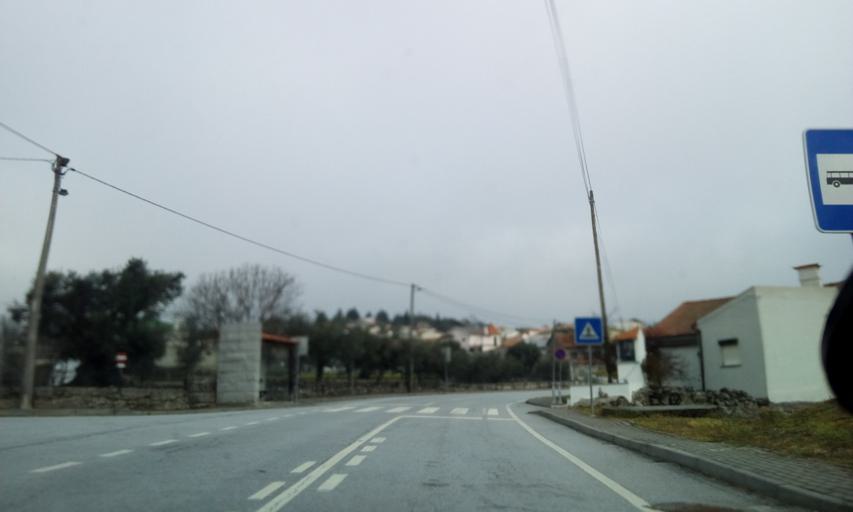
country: PT
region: Guarda
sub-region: Fornos de Algodres
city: Fornos de Algodres
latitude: 40.6828
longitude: -7.4708
